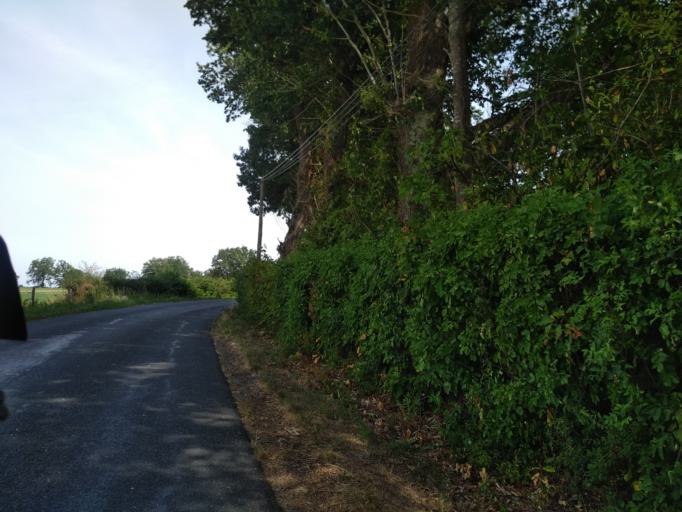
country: FR
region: Auvergne
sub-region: Departement de l'Allier
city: Molinet
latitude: 46.4288
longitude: 3.9742
